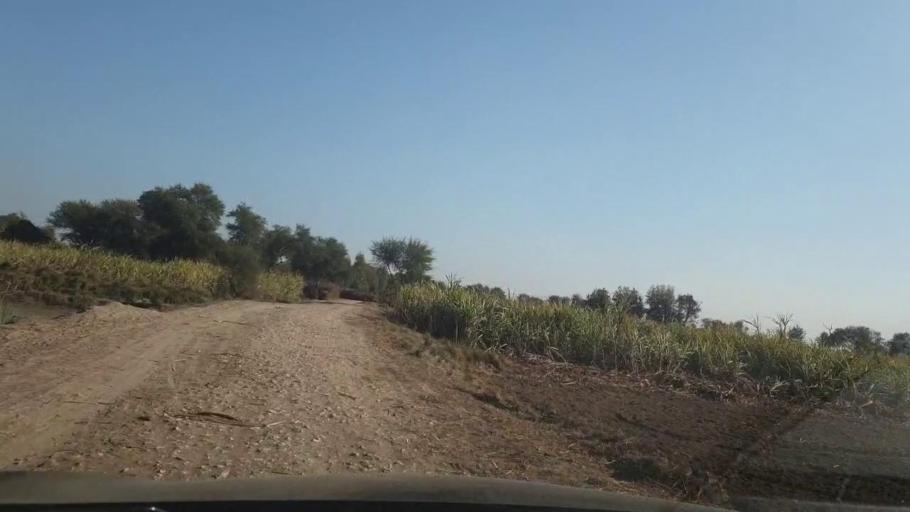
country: PK
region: Sindh
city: Khairpur
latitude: 28.1349
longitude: 69.6056
